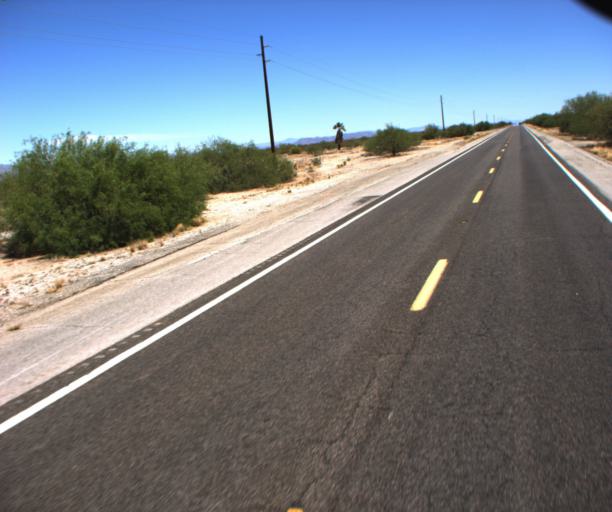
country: US
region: Arizona
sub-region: La Paz County
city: Salome
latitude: 33.8683
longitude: -113.3986
